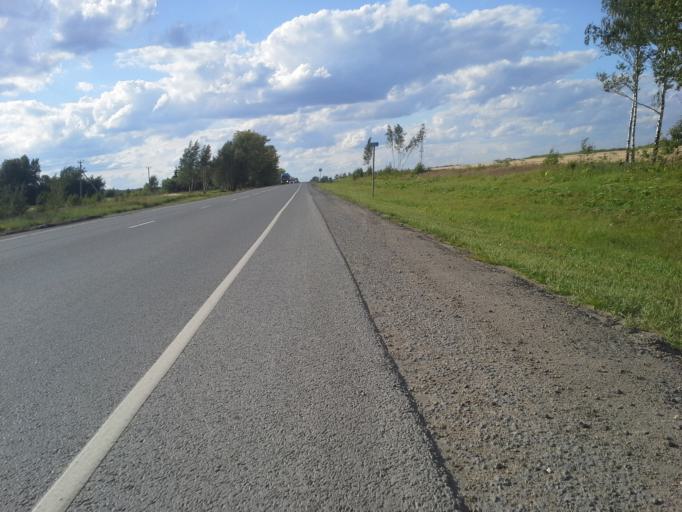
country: RU
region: Moskovskaya
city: Klimovsk
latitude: 55.3554
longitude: 37.4401
